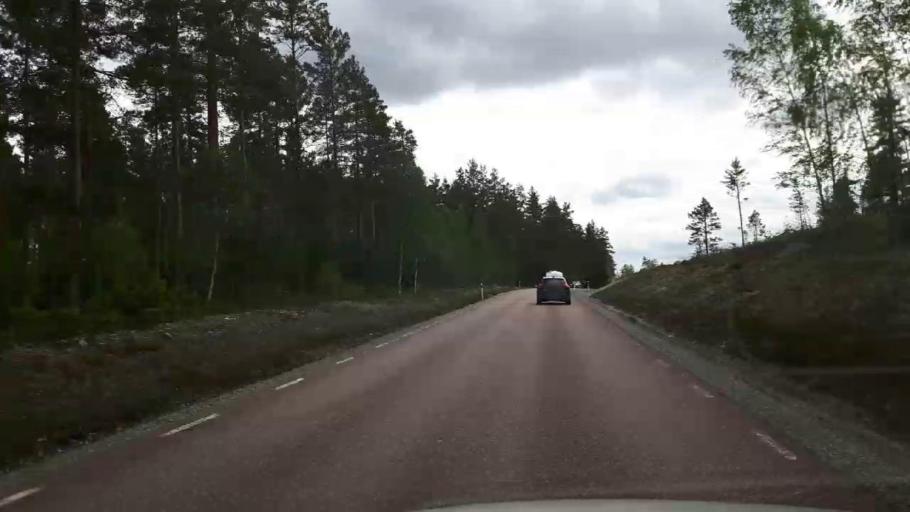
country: SE
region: Vaestmanland
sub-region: Skinnskattebergs Kommun
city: Skinnskatteberg
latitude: 59.8092
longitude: 15.8414
